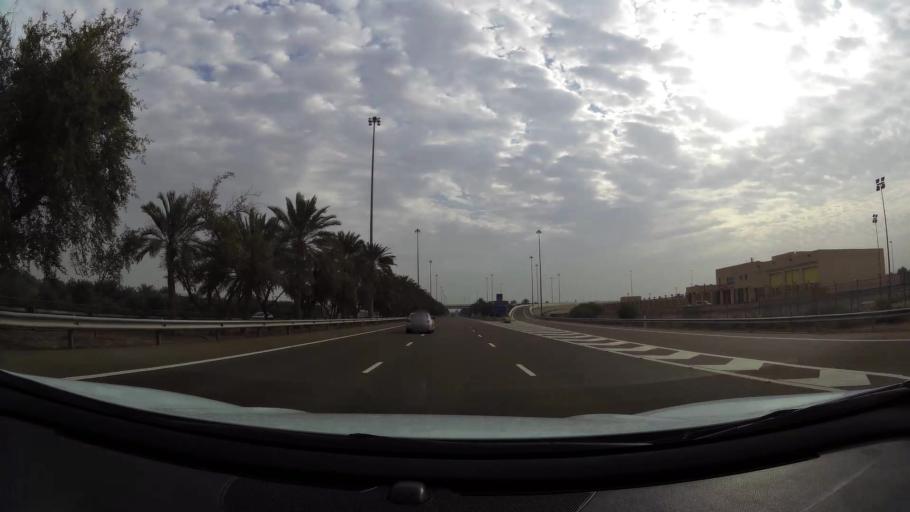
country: AE
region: Abu Dhabi
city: Al Ain
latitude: 24.1816
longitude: 55.3258
